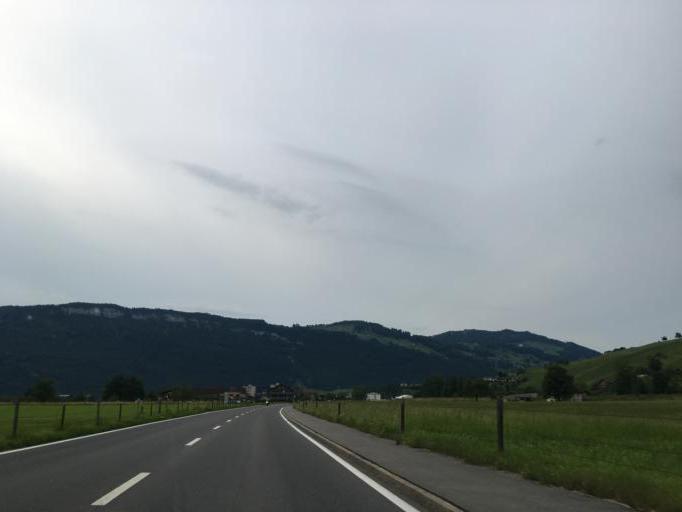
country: CH
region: Nidwalden
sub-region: Nidwalden
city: Dallenwil
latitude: 46.9465
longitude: 8.3883
